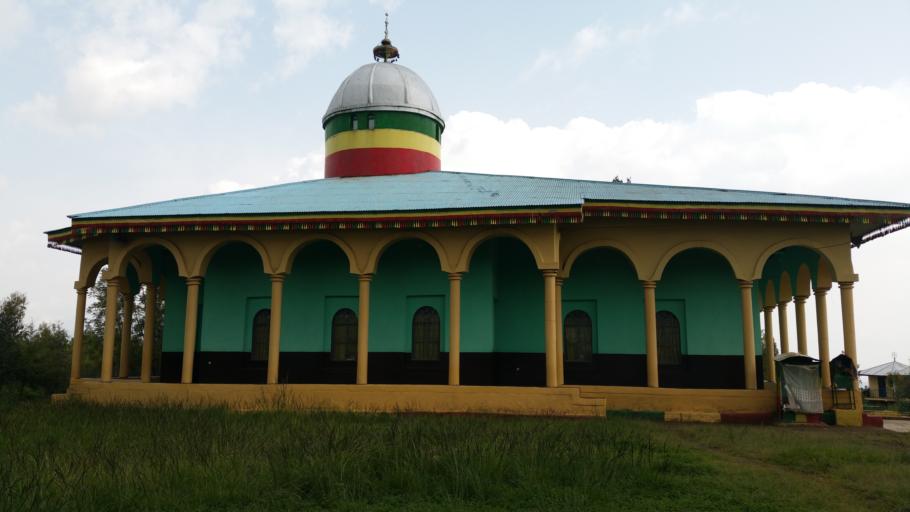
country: ET
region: Amhara
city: Gondar
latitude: 12.6225
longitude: 37.4784
